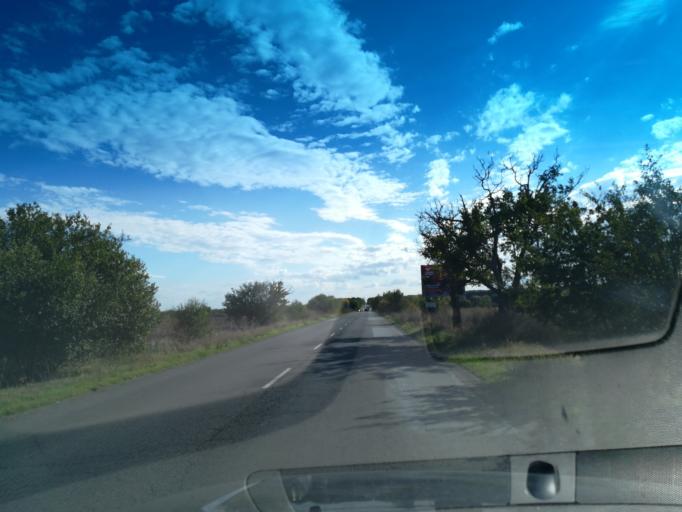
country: BG
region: Stara Zagora
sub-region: Obshtina Stara Zagora
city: Stara Zagora
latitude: 42.3650
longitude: 25.6547
